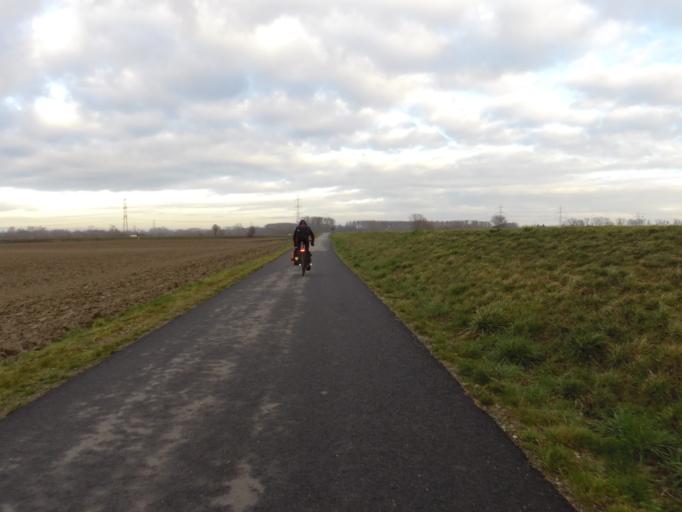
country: DE
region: Rheinland-Pfalz
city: Bobenheim-Roxheim
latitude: 49.5829
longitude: 8.4089
